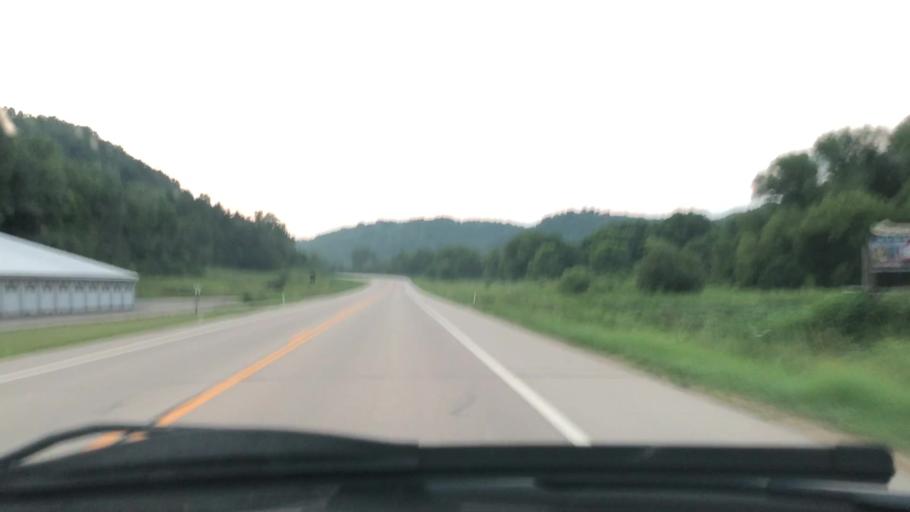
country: US
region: Wisconsin
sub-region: Richland County
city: Richland Center
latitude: 43.3658
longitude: -90.5600
